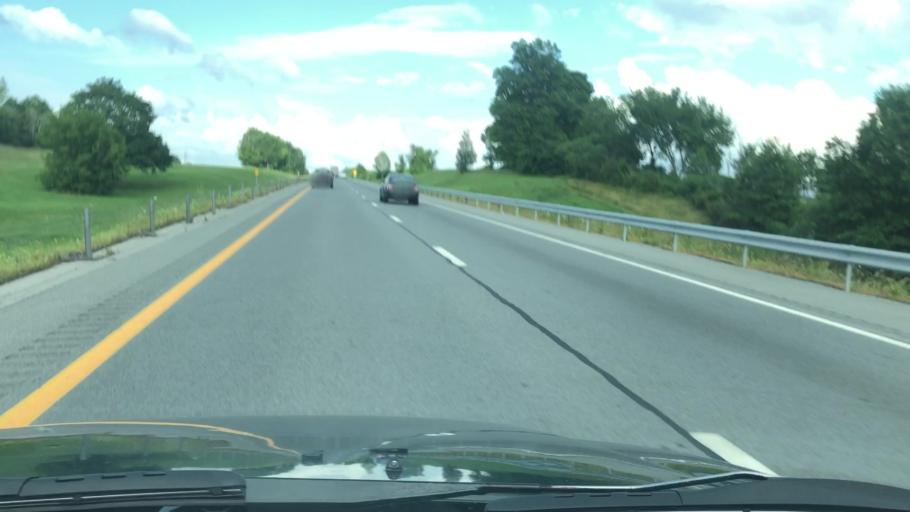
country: US
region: New York
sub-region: Orange County
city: Montgomery
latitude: 41.4990
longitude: -74.2482
